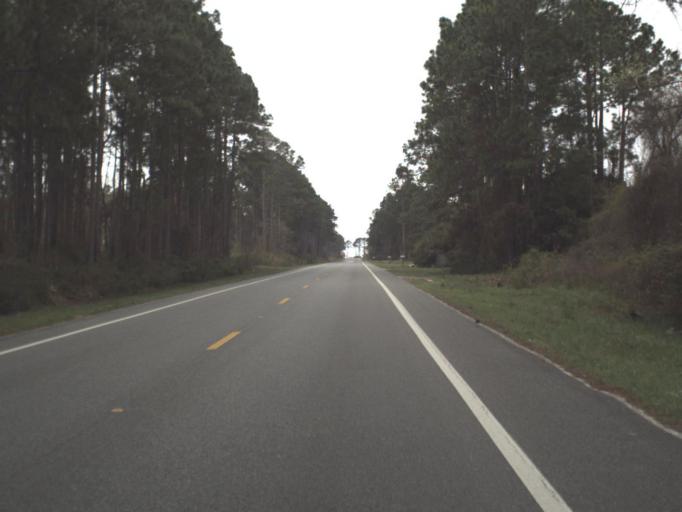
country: US
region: Florida
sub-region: Franklin County
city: Eastpoint
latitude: 29.7668
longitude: -84.8326
